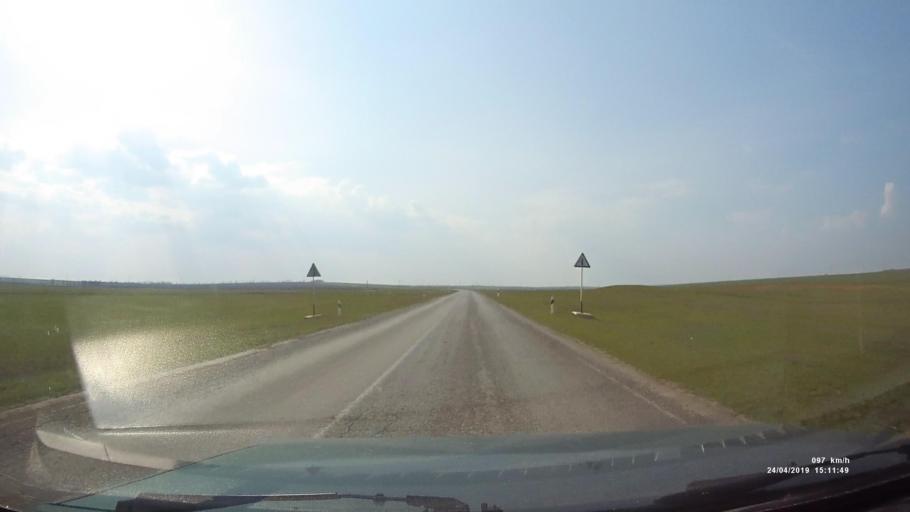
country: RU
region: Rostov
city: Remontnoye
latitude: 46.5448
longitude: 43.3138
